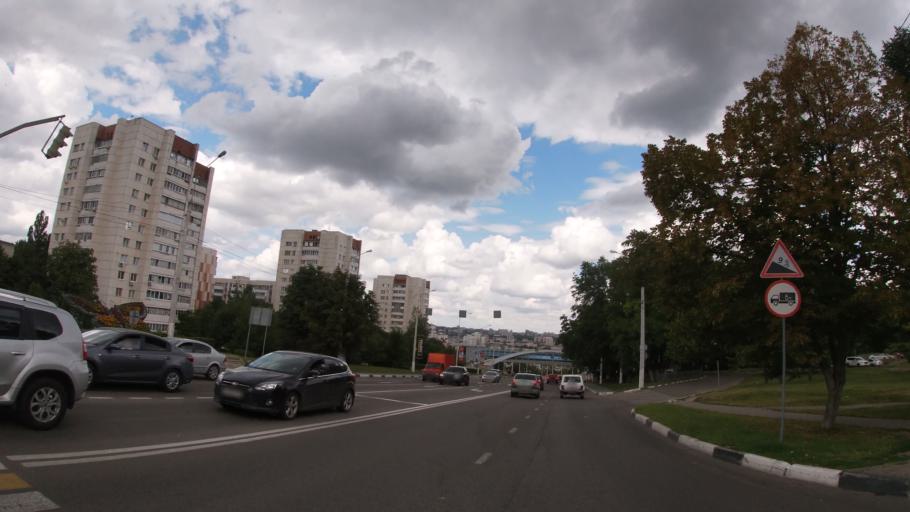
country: RU
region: Belgorod
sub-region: Belgorodskiy Rayon
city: Belgorod
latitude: 50.5788
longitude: 36.5828
